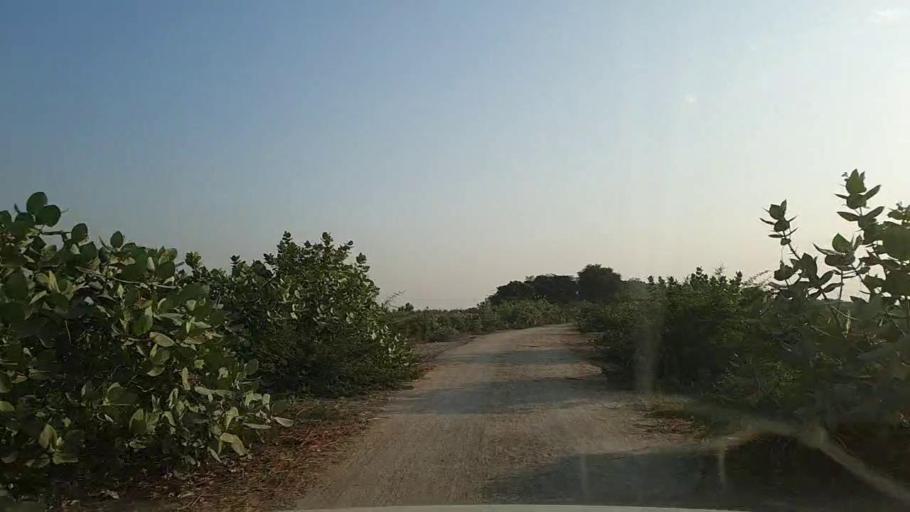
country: PK
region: Sindh
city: Daro Mehar
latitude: 24.7670
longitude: 68.1935
